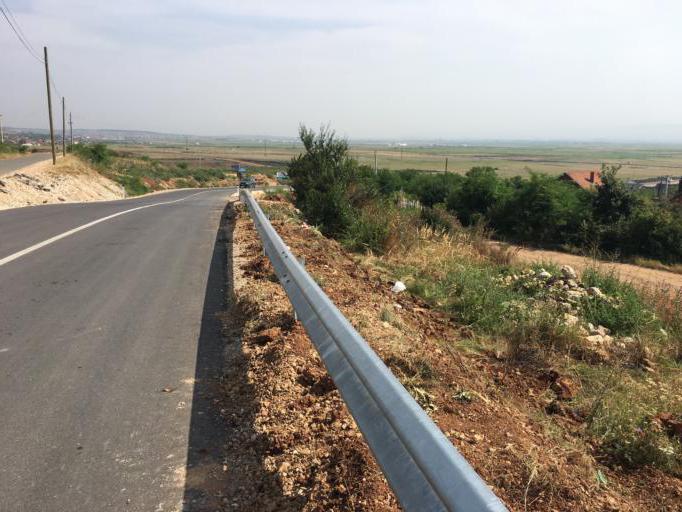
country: XK
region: Pristina
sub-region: Komuna e Gracanices
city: Glanica
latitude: 42.5419
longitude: 21.0141
